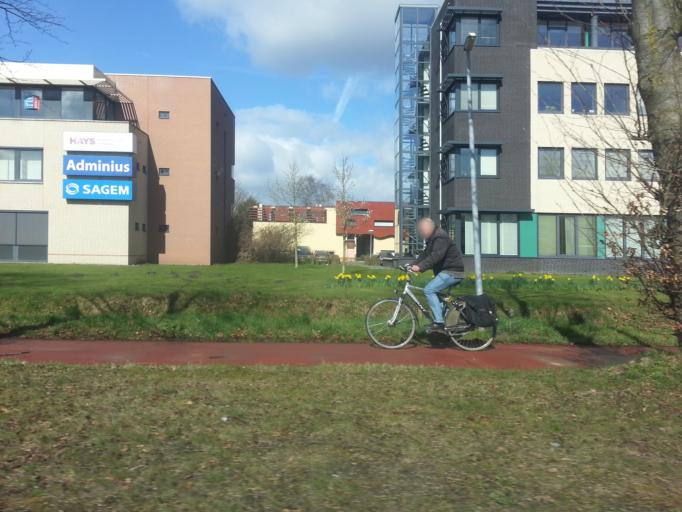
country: NL
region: North Brabant
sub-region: Gemeente Veldhoven
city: Veldhoven
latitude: 51.4279
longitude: 5.4118
